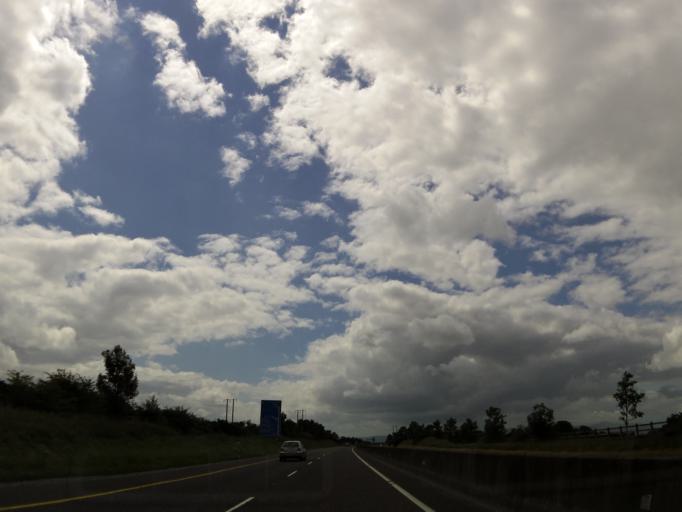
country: IE
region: Munster
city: Cashel
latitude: 52.5188
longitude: -7.8608
